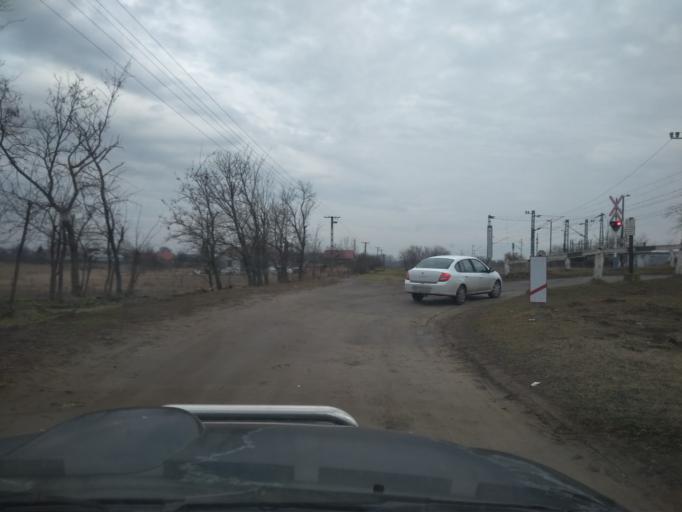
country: HU
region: Szabolcs-Szatmar-Bereg
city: Nyiregyhaza
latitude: 47.9672
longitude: 21.6852
